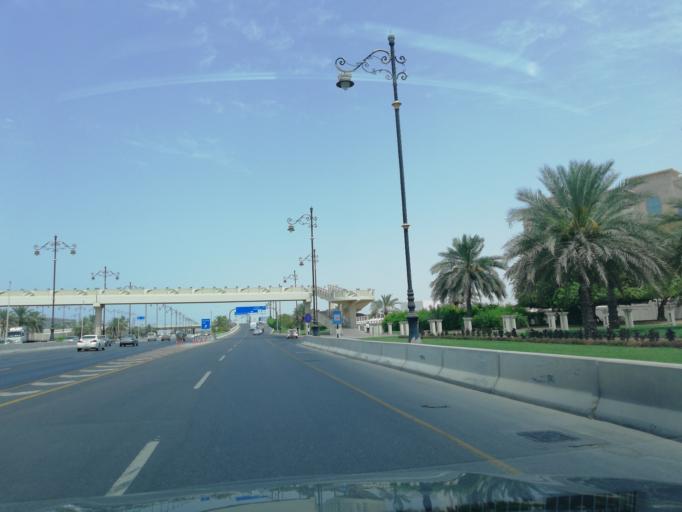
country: OM
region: Muhafazat Masqat
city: Bawshar
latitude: 23.5858
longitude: 58.2909
